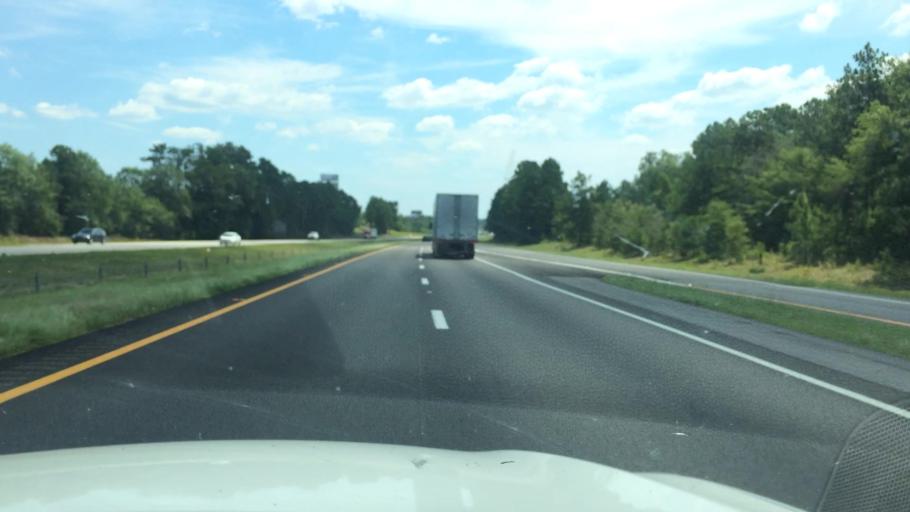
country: US
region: South Carolina
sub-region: Aiken County
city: Aiken
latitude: 33.6680
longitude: -81.6703
